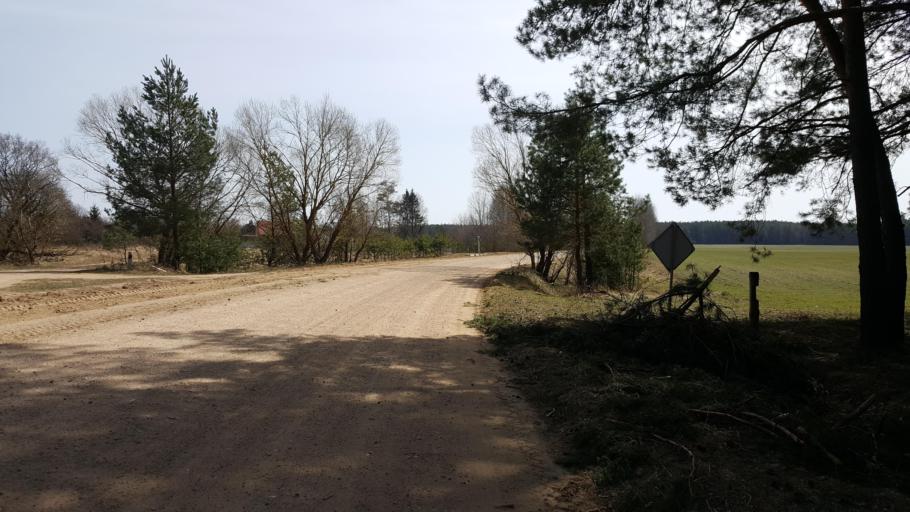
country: BY
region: Brest
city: Kamyanyuki
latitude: 52.5696
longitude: 23.7527
